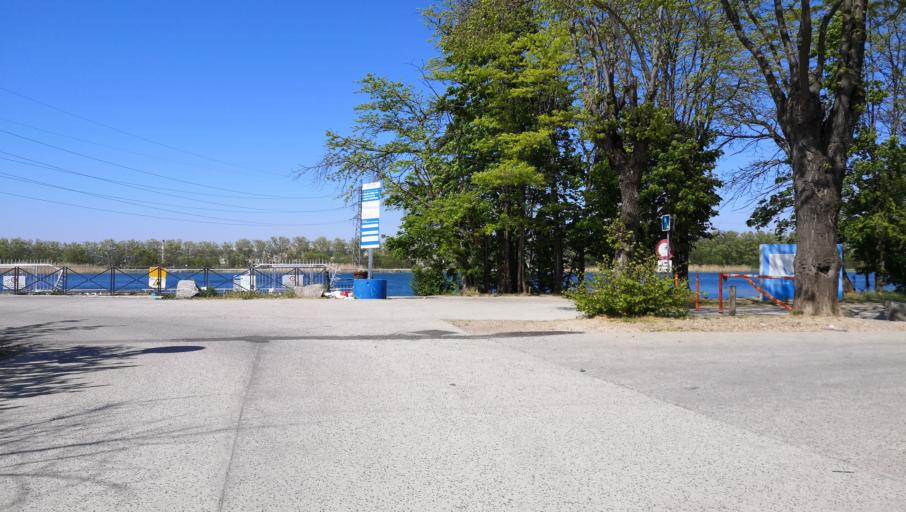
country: FR
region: Rhone-Alpes
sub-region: Departement du Rhone
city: Vaulx-en-Velin
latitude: 45.7668
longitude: 4.9183
